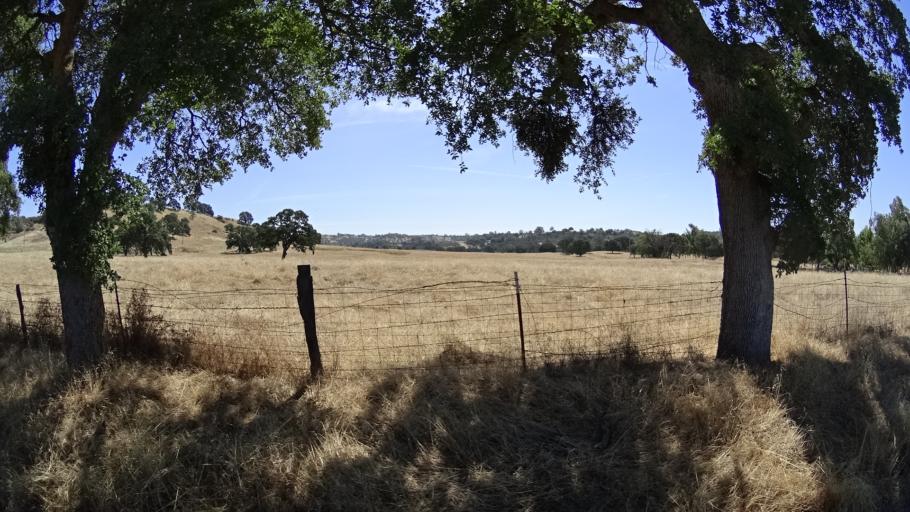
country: US
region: California
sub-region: Calaveras County
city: Rancho Calaveras
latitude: 38.1641
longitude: -120.8913
